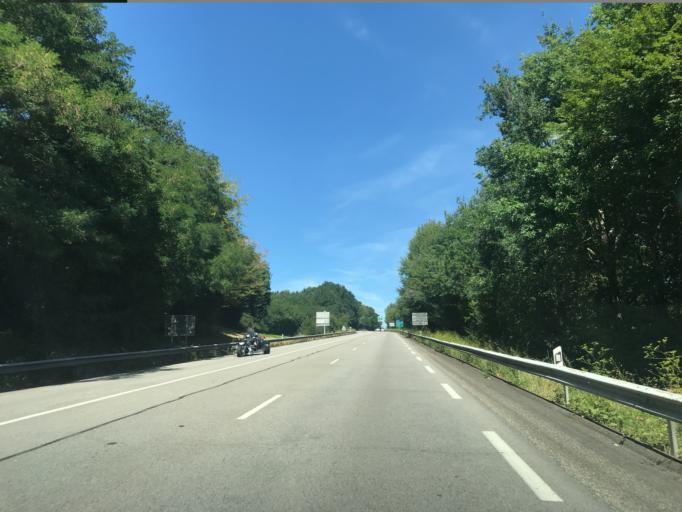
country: FR
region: Limousin
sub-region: Departement de la Correze
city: Tulle
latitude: 45.2681
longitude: 1.7910
